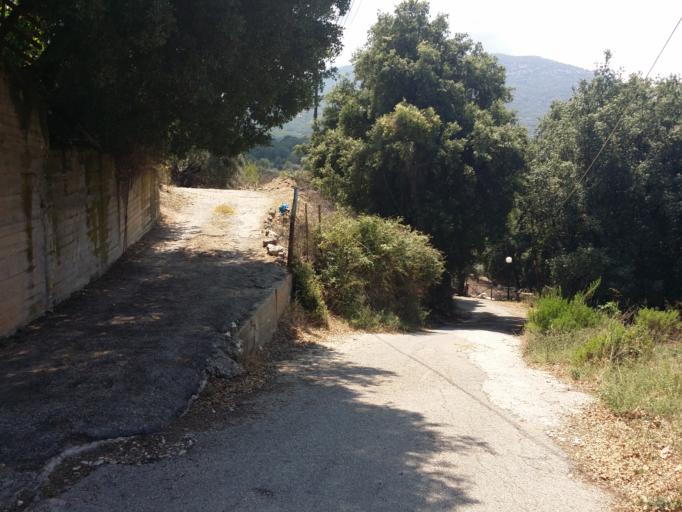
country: GR
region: West Greece
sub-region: Nomos Aitolias kai Akarnanias
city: Monastirakion
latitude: 38.8619
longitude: 20.9543
